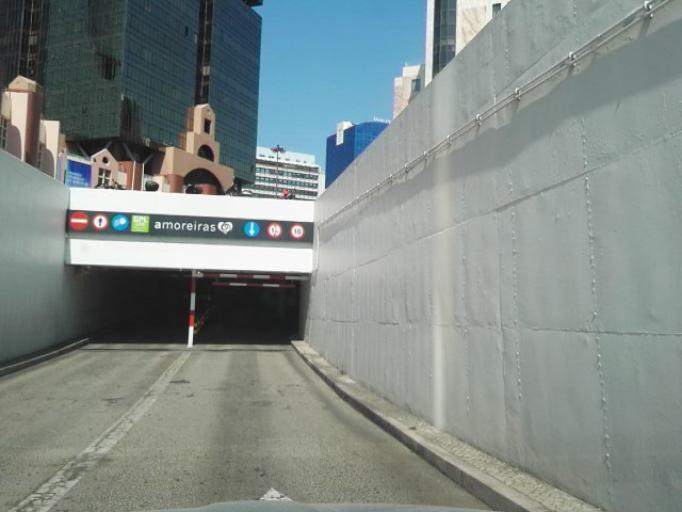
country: PT
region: Lisbon
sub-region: Lisbon
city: Lisbon
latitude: 38.7228
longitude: -9.1612
